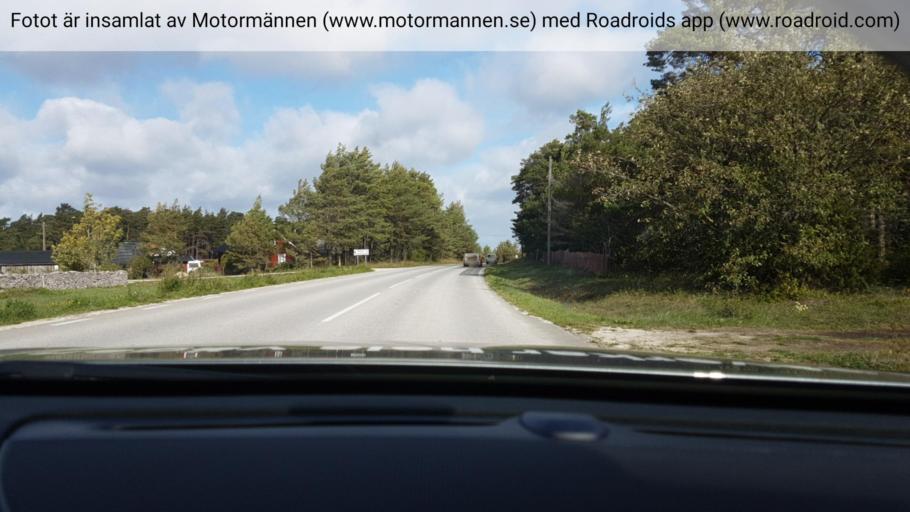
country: SE
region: Gotland
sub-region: Gotland
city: Slite
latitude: 57.8972
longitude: 19.0926
